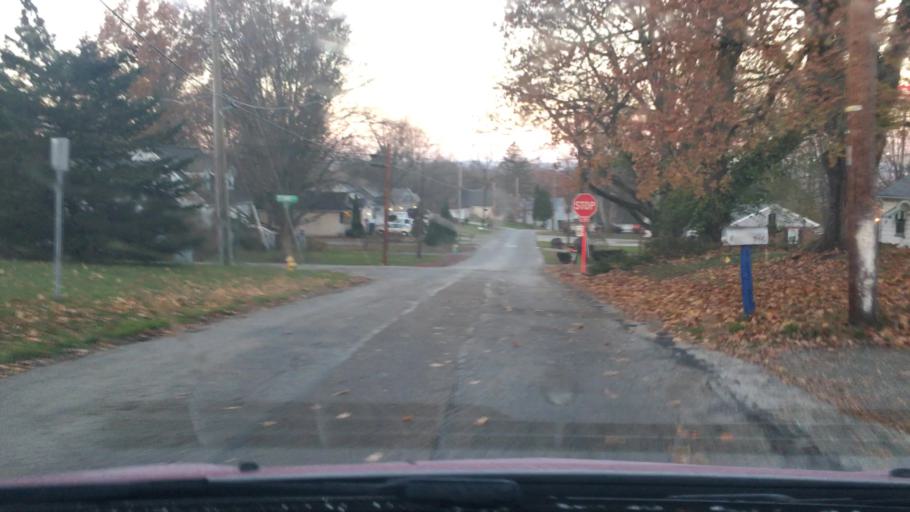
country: US
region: Ohio
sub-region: Wayne County
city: Wooster
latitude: 40.7876
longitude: -81.9302
